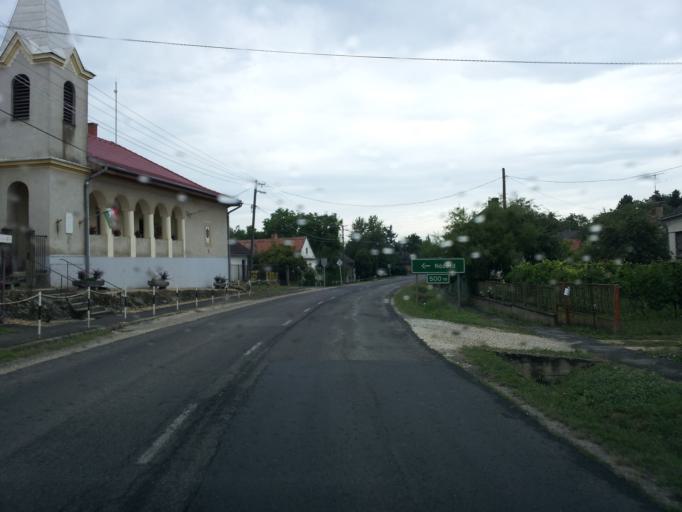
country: HU
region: Vas
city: Kormend
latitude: 46.9589
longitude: 16.6421
